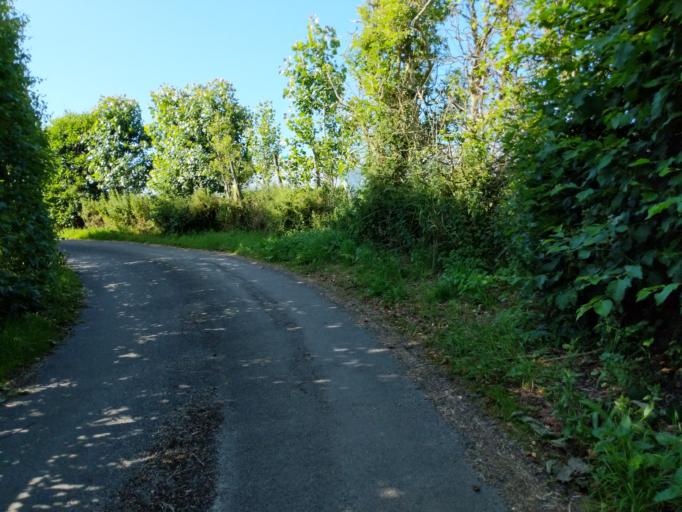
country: GB
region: England
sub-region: Kent
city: Faversham
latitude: 51.3278
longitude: 0.9332
